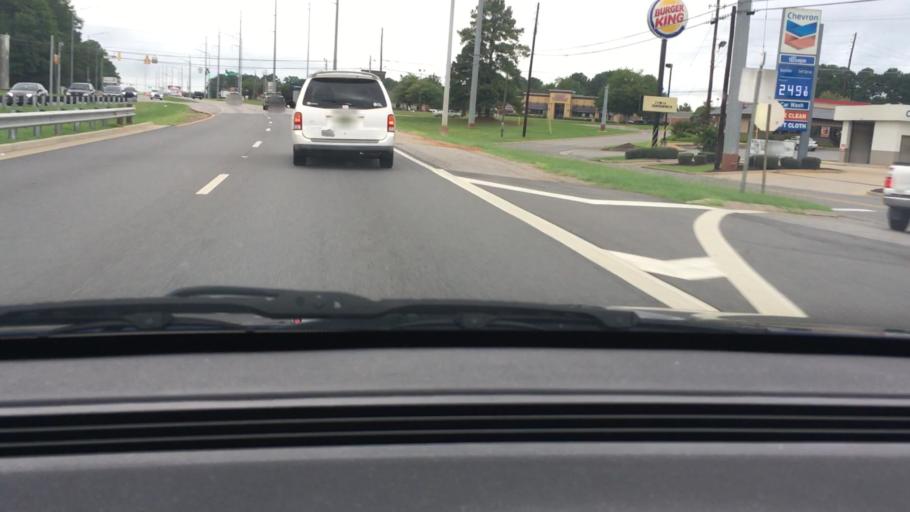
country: US
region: Alabama
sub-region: Tuscaloosa County
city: Tuscaloosa
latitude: 33.2327
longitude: -87.5378
